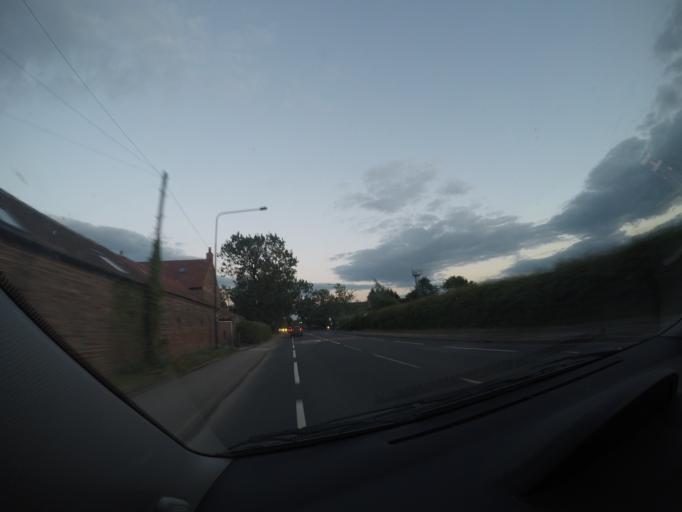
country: GB
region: England
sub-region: City of York
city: Haxby
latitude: 53.9991
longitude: -1.0725
